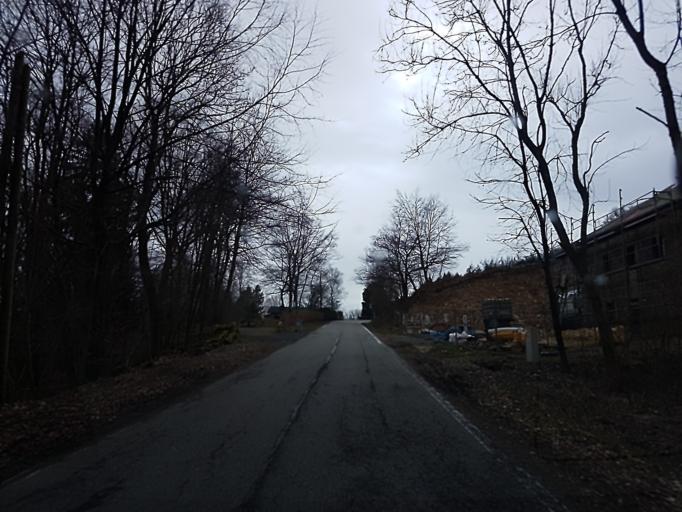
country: BE
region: Wallonia
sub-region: Province de Liege
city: Stoumont
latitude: 50.4182
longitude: 5.8085
